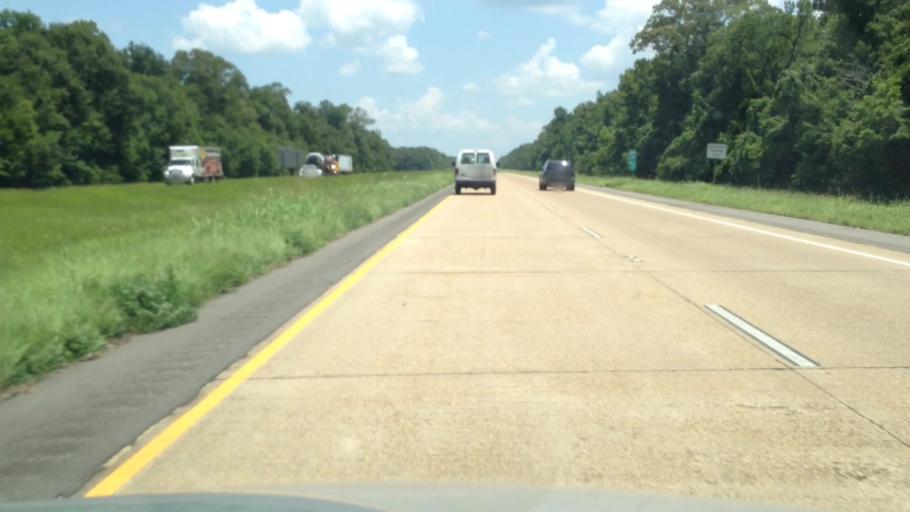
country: US
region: Louisiana
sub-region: Rapides Parish
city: Lecompte
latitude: 31.0006
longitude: -92.3410
